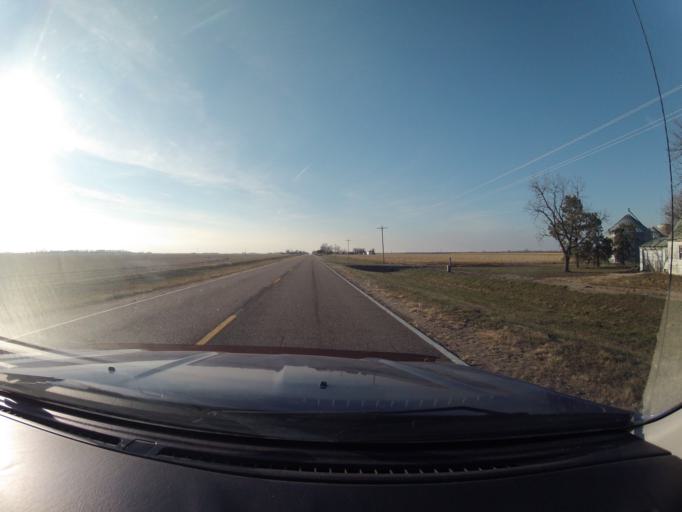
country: US
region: Nebraska
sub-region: Buffalo County
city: Kearney
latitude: 40.6410
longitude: -98.9743
